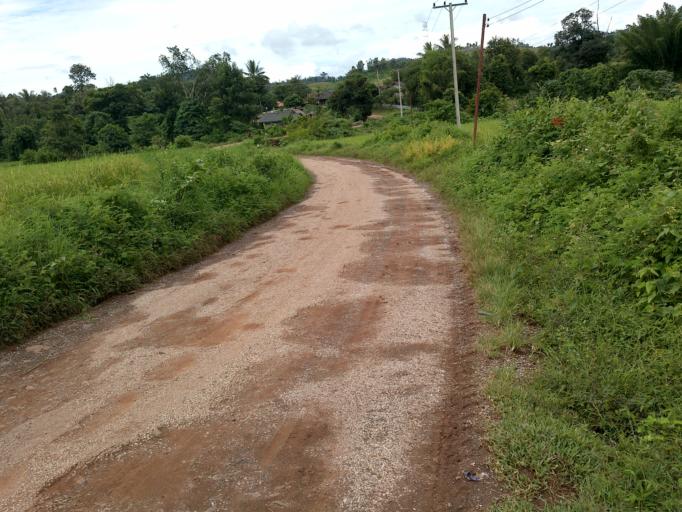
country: LA
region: Xiagnabouli
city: Sainyabuli
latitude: 19.0762
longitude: 101.6291
